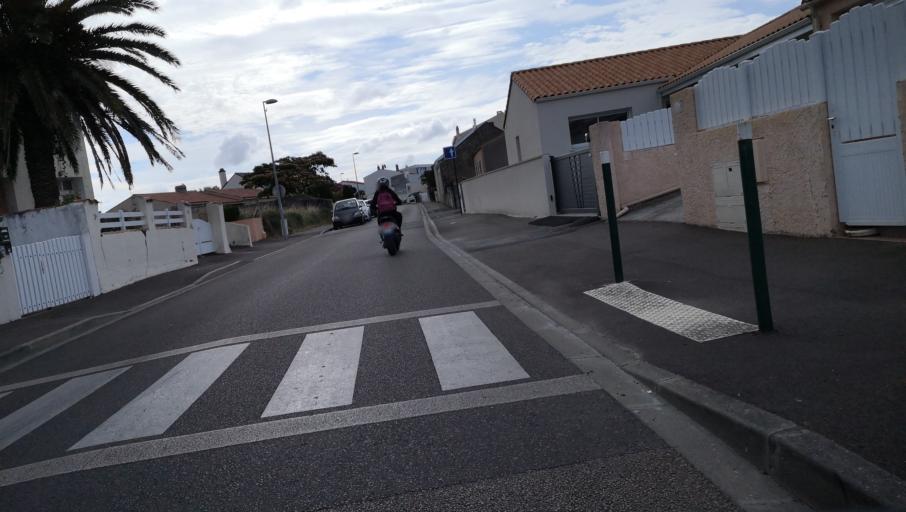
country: FR
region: Pays de la Loire
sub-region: Departement de la Vendee
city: Les Sables-d'Olonne
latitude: 46.5067
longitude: -1.7830
